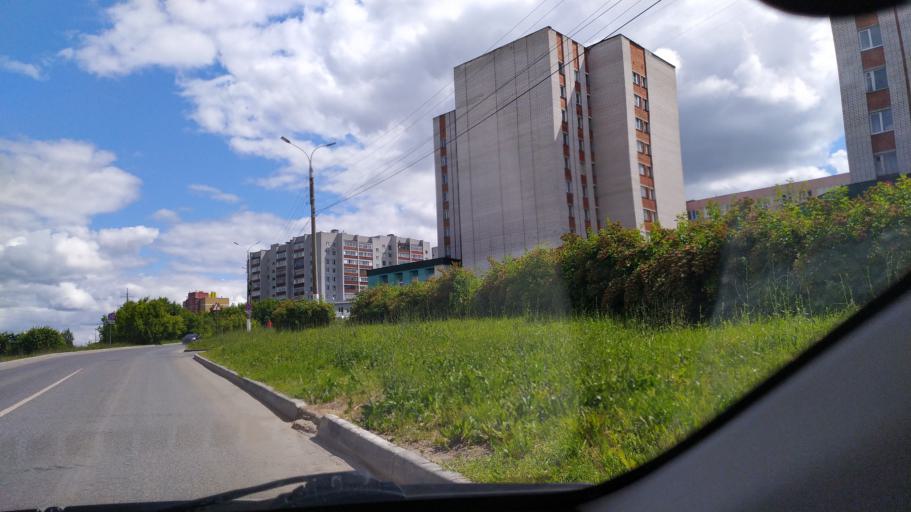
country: RU
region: Chuvashia
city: Novyye Lapsary
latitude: 56.1238
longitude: 47.1842
